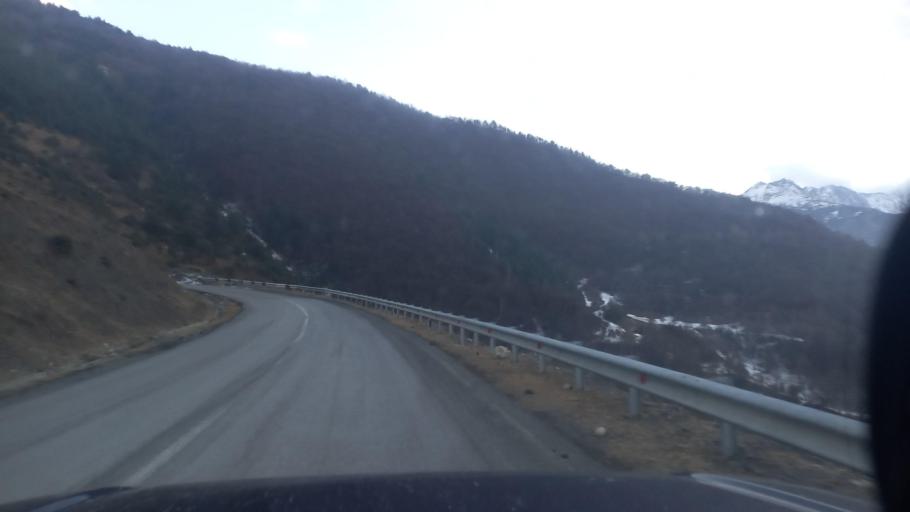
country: RU
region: Ingushetiya
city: Dzhayrakh
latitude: 42.8098
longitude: 44.7982
